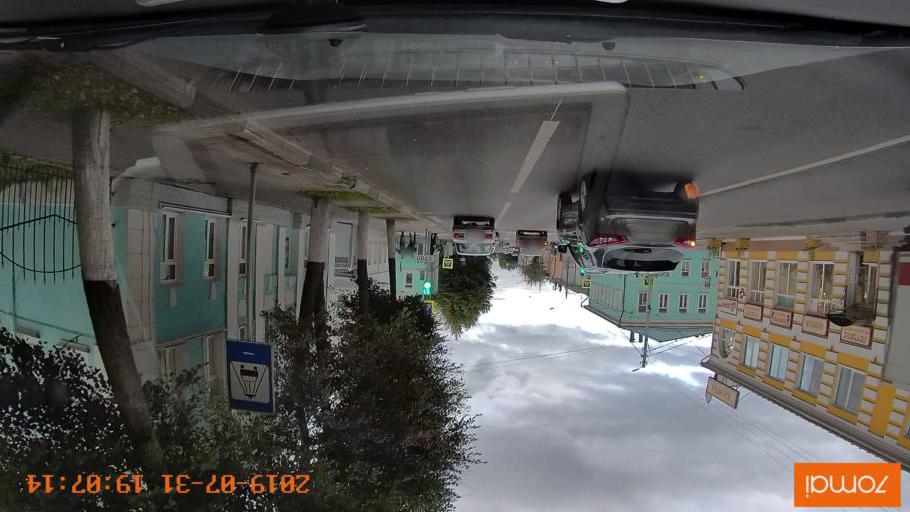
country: RU
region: Moskovskaya
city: Kolomna
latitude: 55.0991
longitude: 38.7592
